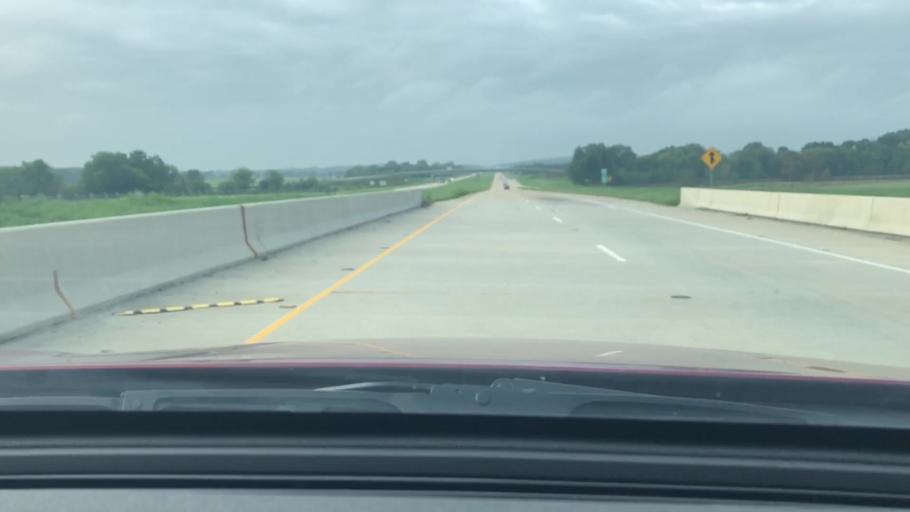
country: US
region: Louisiana
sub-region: Caddo Parish
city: Vivian
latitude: 32.8507
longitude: -93.8651
